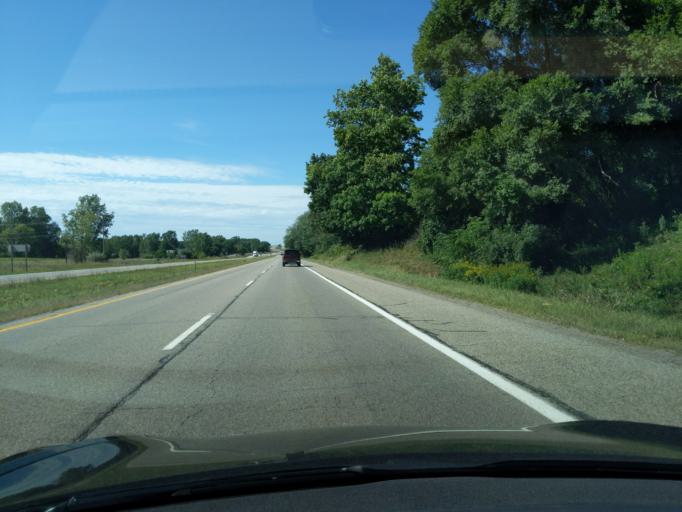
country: US
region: Michigan
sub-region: Eaton County
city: Dimondale
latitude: 42.6631
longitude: -84.6737
